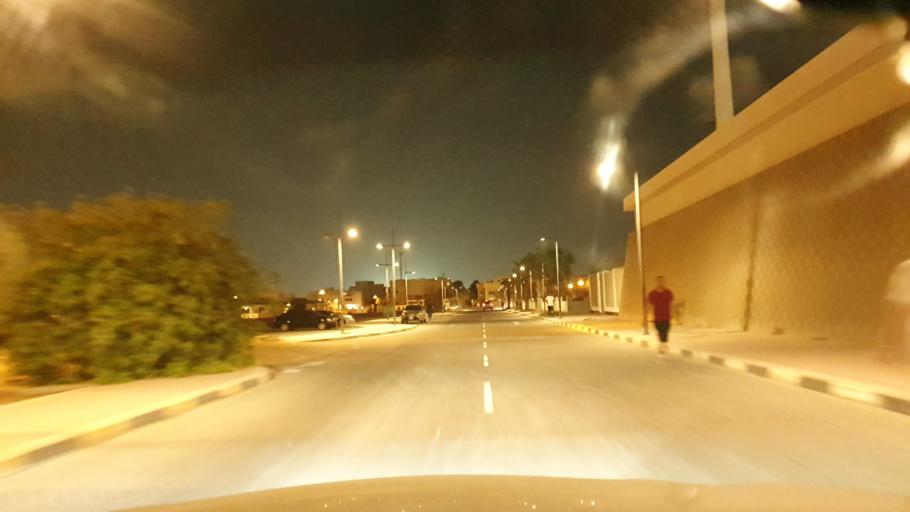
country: BH
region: Northern
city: Madinat `Isa
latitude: 26.1554
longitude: 50.5461
